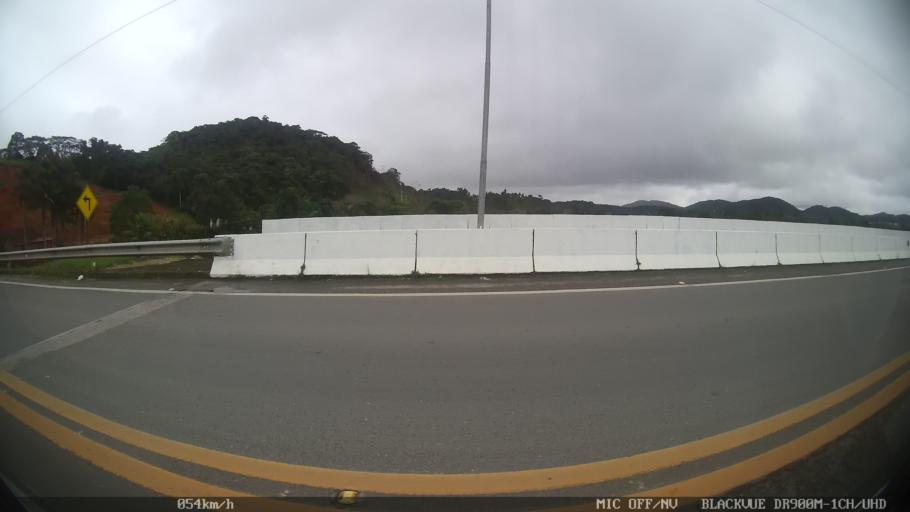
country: BR
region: Sao Paulo
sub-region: Juquia
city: Juquia
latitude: -24.3326
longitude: -47.6353
